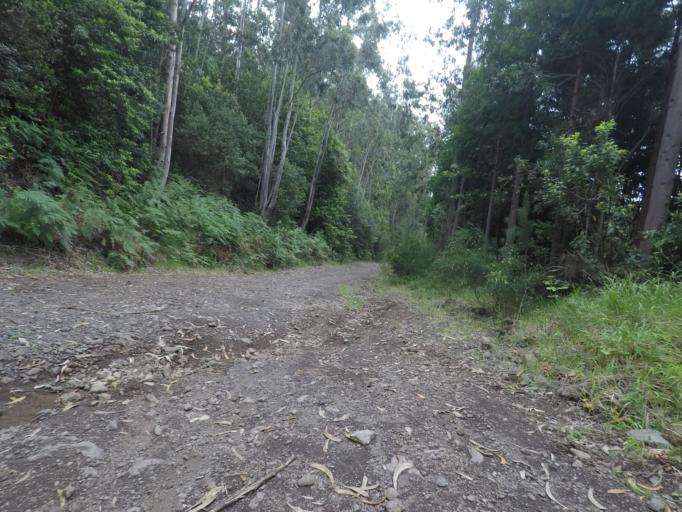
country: PT
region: Madeira
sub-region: Sao Vicente
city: Sao Vicente
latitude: 32.7738
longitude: -17.0478
